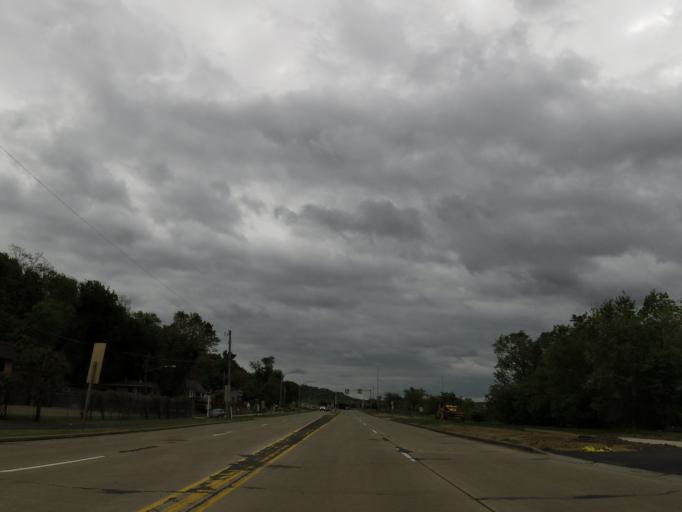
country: US
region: Wisconsin
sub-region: Saint Croix County
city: Hudson
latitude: 44.9666
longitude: -92.7553
